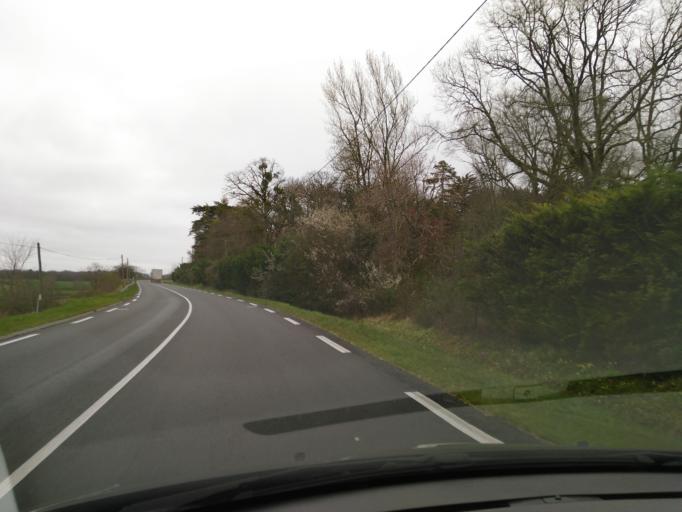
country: FR
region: Aquitaine
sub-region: Departement de la Dordogne
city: Monbazillac
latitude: 44.7432
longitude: 0.5391
